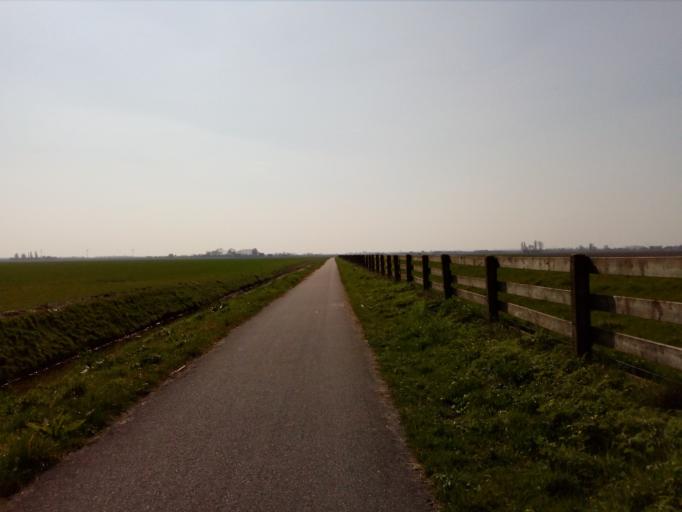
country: NL
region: South Holland
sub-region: Gemeente Waddinxveen
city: Groenswaard
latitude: 52.0607
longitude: 4.6080
